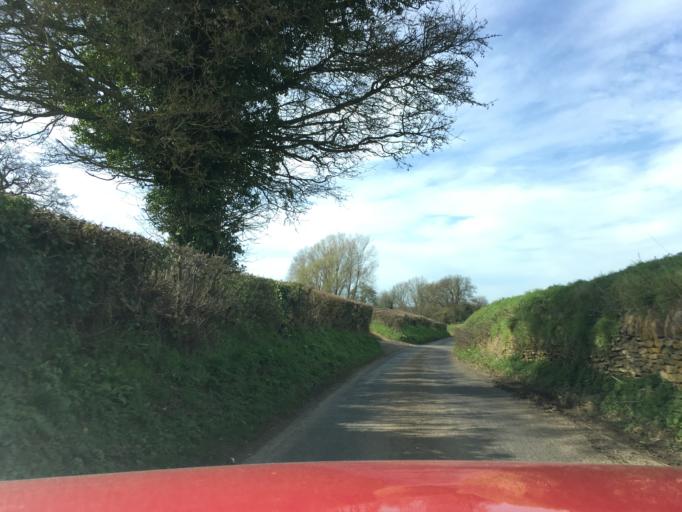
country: GB
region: England
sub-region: Wiltshire
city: Luckington
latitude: 51.5450
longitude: -2.2376
